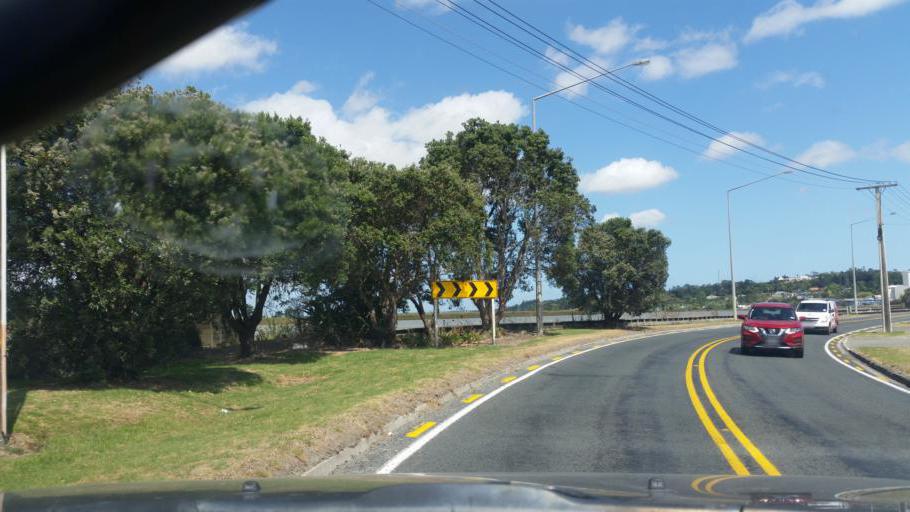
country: NZ
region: Northland
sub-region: Kaipara District
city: Dargaville
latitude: -35.9460
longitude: 173.8667
